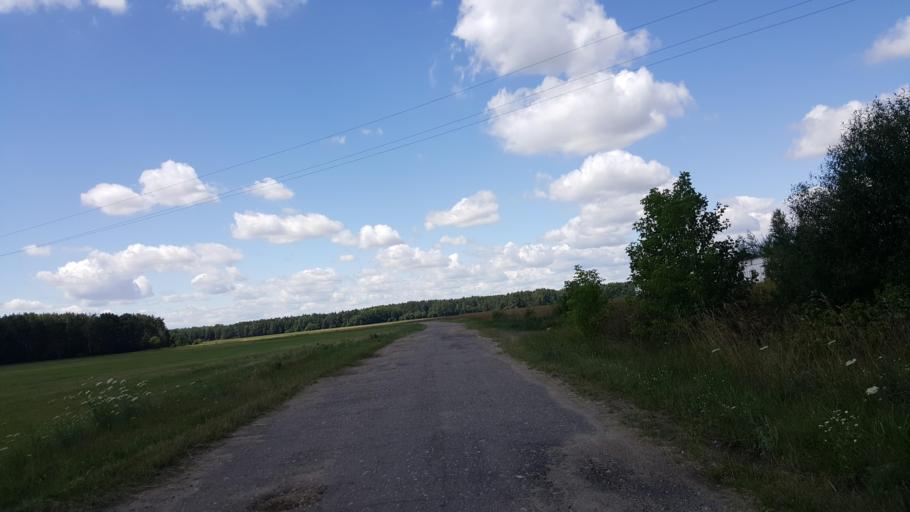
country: BY
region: Brest
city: Kamyanyets
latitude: 52.3324
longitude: 23.9073
